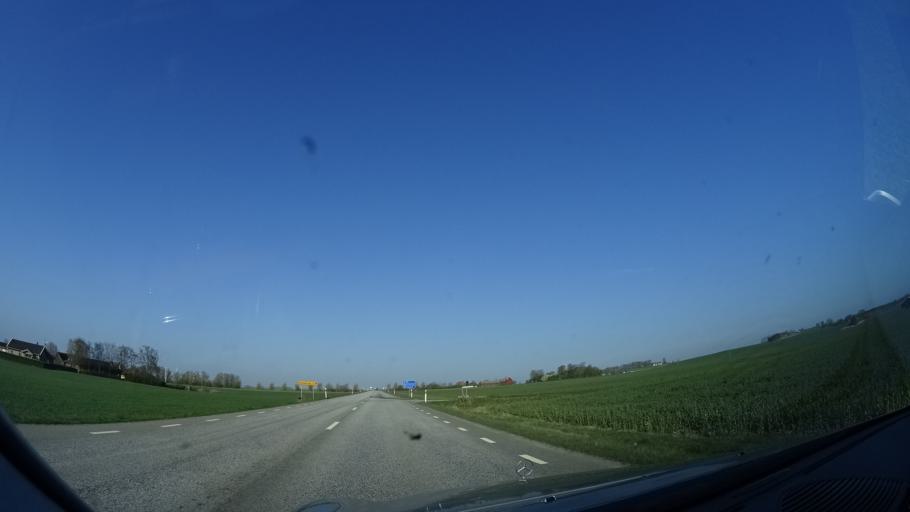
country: SE
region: Skane
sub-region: Landskrona
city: Asmundtorp
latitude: 55.8908
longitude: 12.9495
